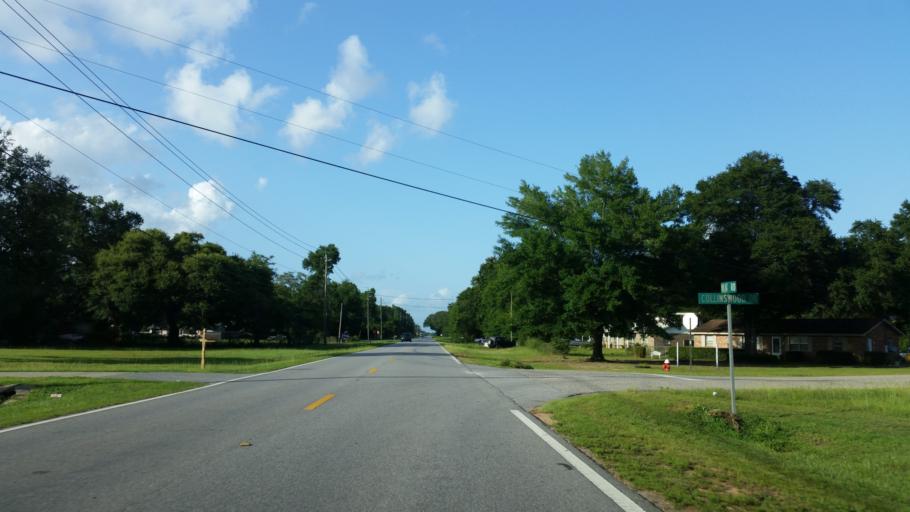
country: US
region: Florida
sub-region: Santa Rosa County
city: Bagdad
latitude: 30.5802
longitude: -87.0922
